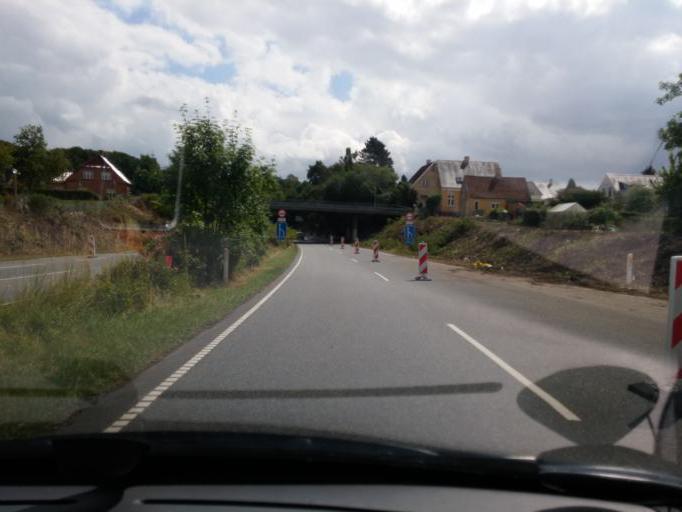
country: DK
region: South Denmark
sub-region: Svendborg Kommune
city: Svendborg
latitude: 55.0574
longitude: 10.5900
